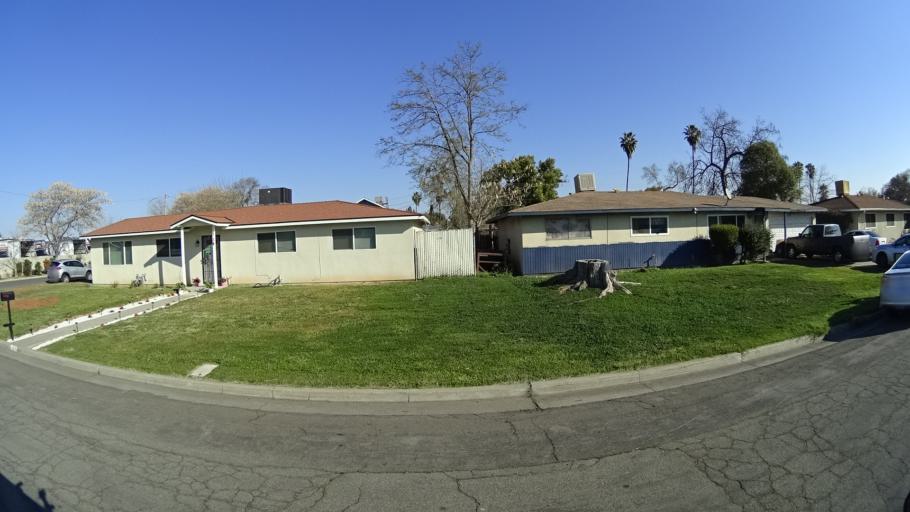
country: US
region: California
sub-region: Fresno County
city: Fresno
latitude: 36.8248
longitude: -119.7878
